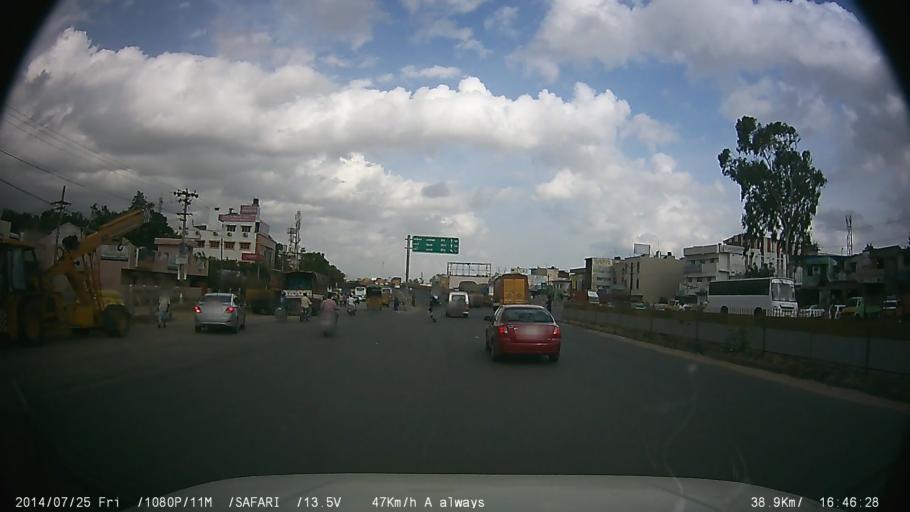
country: IN
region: Tamil Nadu
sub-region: Krishnagiri
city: Hosur
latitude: 12.7372
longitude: 77.8237
